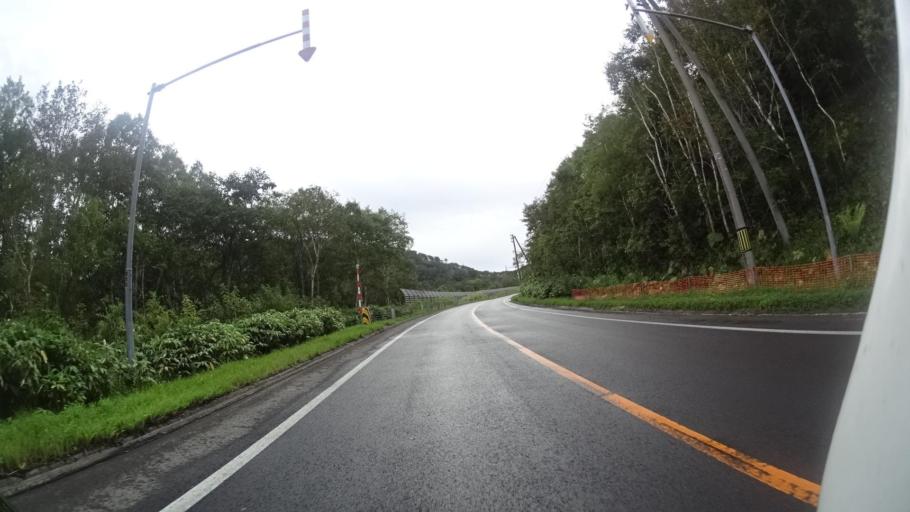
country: JP
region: Hokkaido
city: Shibetsu
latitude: 43.7730
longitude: 144.7964
